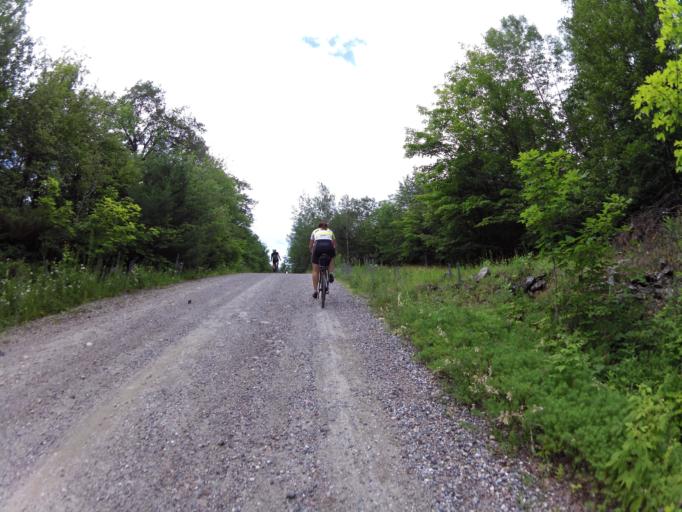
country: CA
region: Ontario
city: Perth
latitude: 45.0257
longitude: -76.5726
